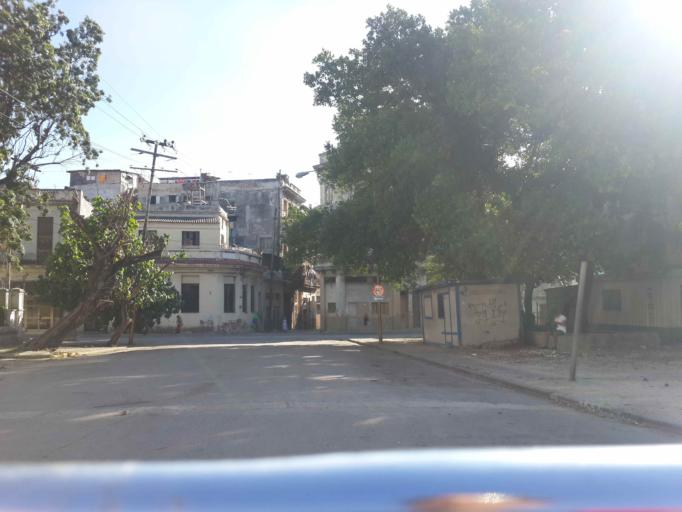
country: CU
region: La Habana
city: La Habana Vieja
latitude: 23.1313
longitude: -82.3554
